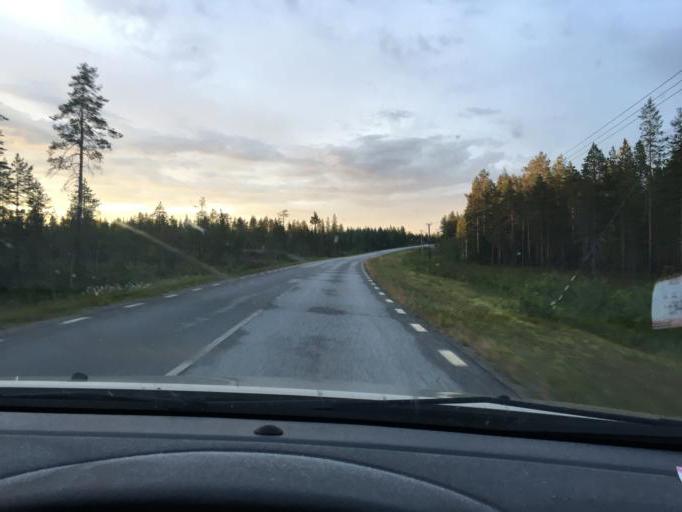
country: SE
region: Norrbotten
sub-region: Kalix Kommun
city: Toere
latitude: 66.0596
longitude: 22.6011
